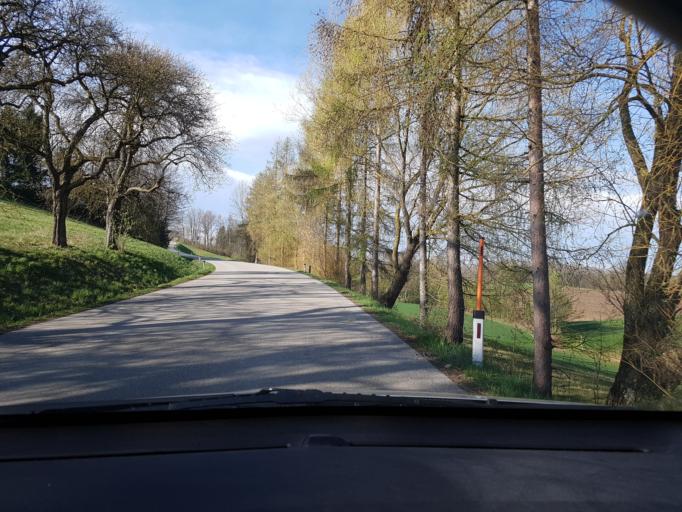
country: AT
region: Upper Austria
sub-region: Politischer Bezirk Linz-Land
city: Sankt Florian
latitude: 48.1521
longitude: 14.3858
